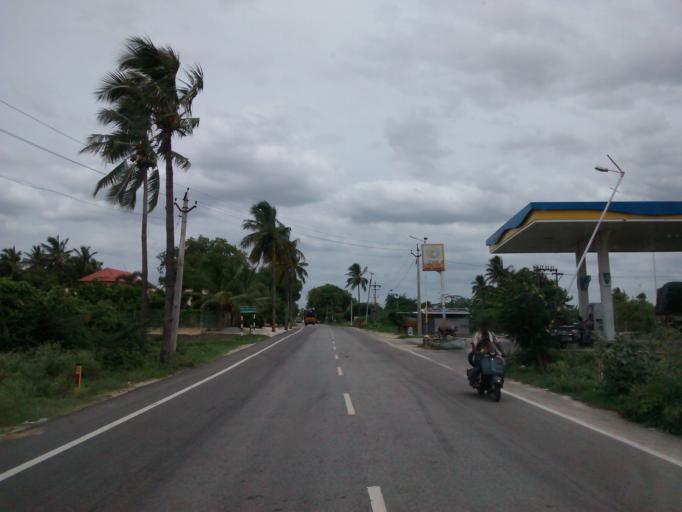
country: IN
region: Andhra Pradesh
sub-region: Chittoor
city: Chittoor
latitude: 13.2881
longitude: 79.0394
